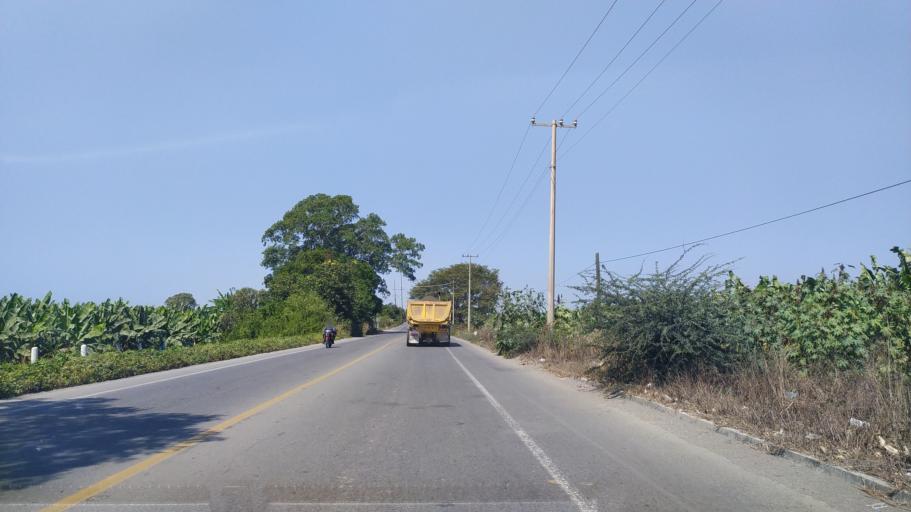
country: MX
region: Michoacan
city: Coahuayana Viejo
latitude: 18.7129
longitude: -103.7124
